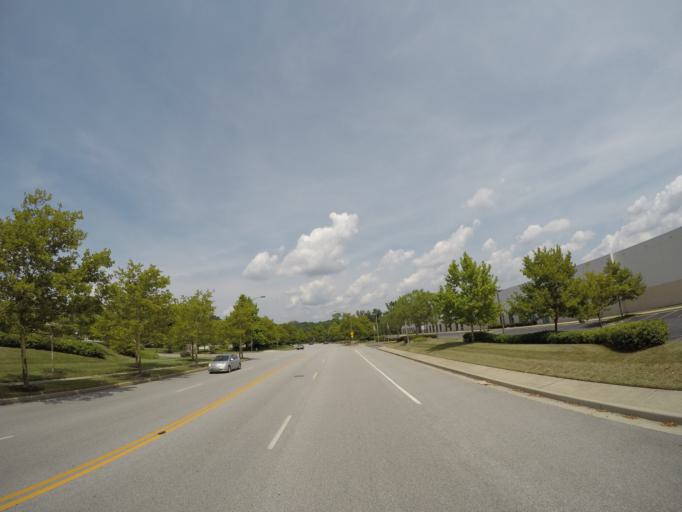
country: US
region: Maryland
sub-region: Howard County
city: Savage
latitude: 39.1320
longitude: -76.8210
